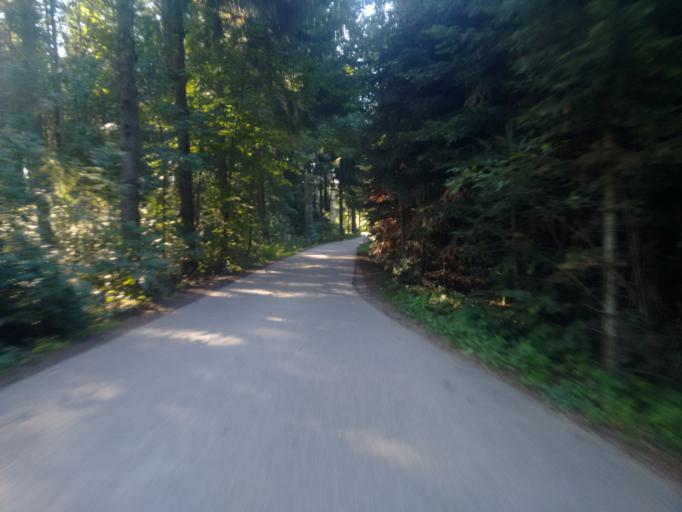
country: AT
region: Upper Austria
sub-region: Wels-Land
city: Buchkirchen
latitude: 48.1936
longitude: 13.9970
